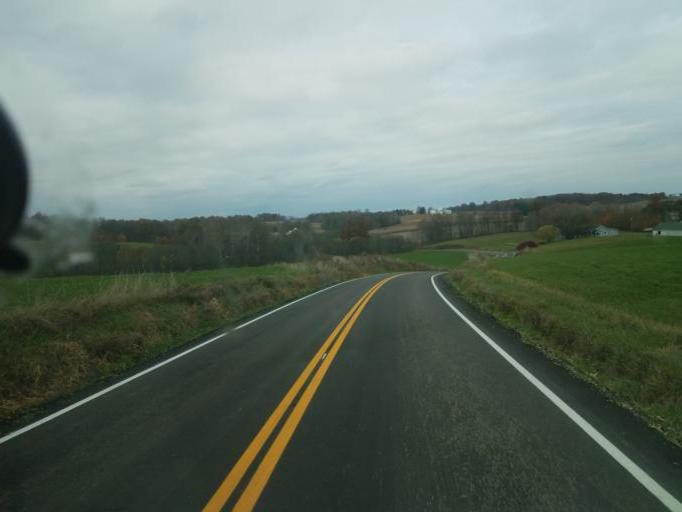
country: US
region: Ohio
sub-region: Wayne County
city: Shreve
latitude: 40.5971
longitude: -82.0614
